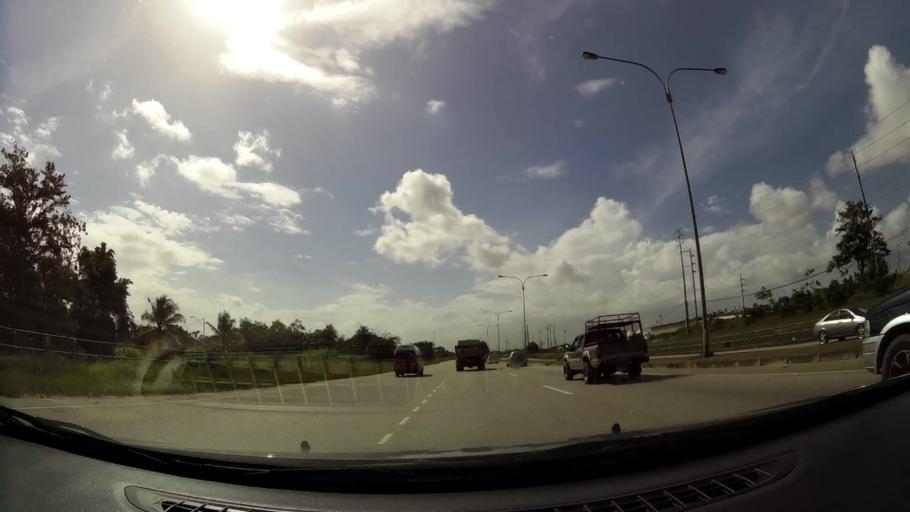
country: TT
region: Borough of Arima
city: Arima
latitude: 10.6074
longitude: -61.2734
